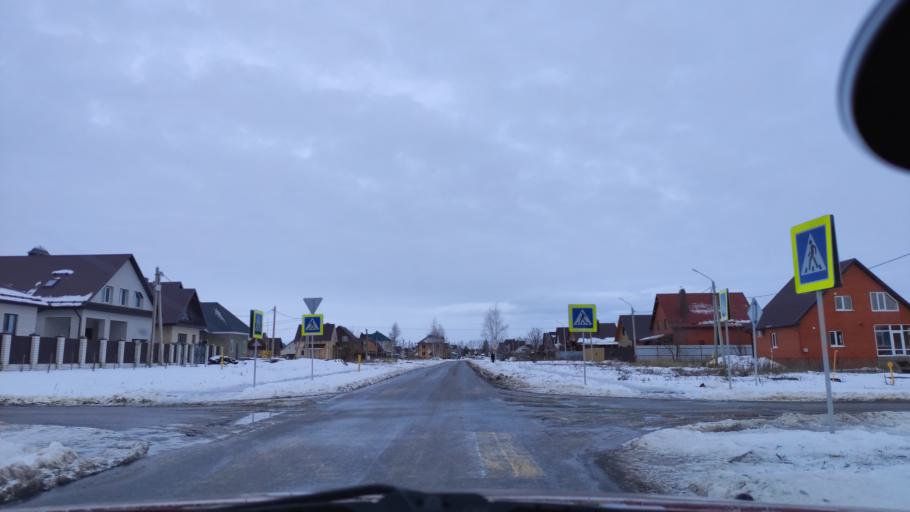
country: RU
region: Tambov
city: Tambov
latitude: 52.7644
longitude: 41.3740
